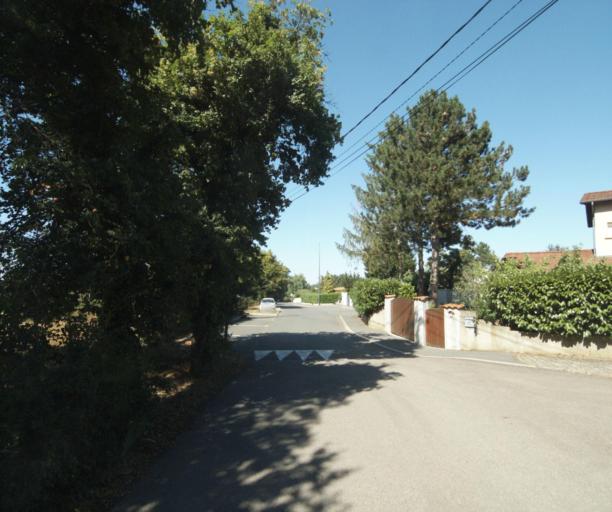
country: FR
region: Rhone-Alpes
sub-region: Departement du Rhone
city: La Tour-de-Salvagny
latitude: 45.8352
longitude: 4.7100
